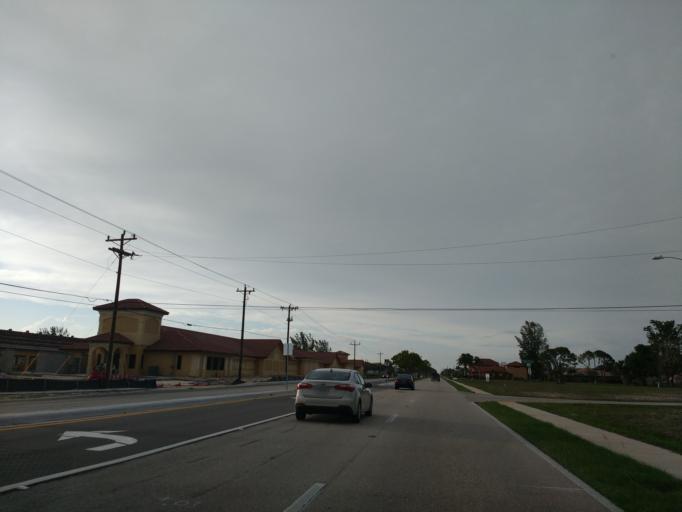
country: US
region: Florida
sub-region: Lee County
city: Cape Coral
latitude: 26.5668
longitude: -82.0067
